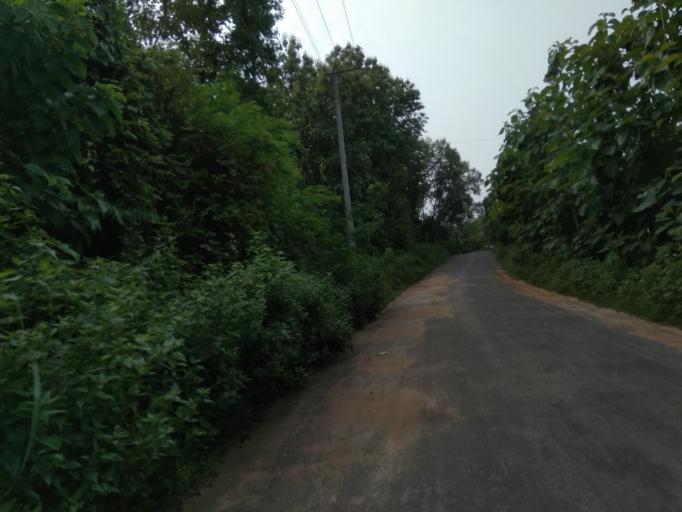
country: BD
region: Chittagong
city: Khagrachhari
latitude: 23.0344
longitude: 92.0078
